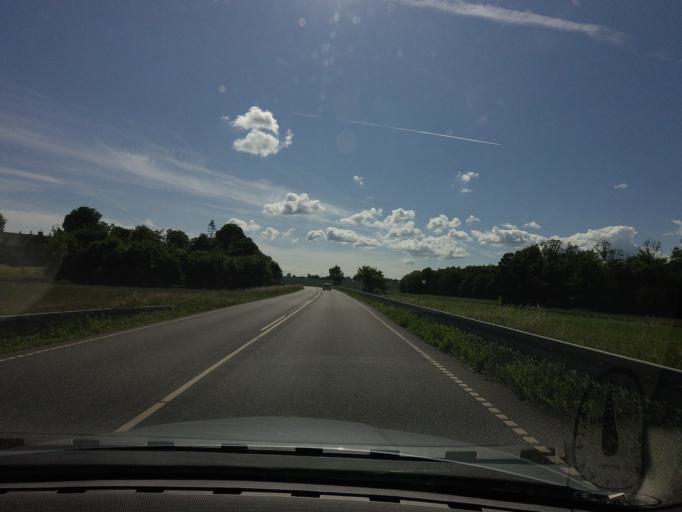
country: DK
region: Central Jutland
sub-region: Syddjurs Kommune
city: Ebeltoft
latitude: 56.3281
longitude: 10.7184
